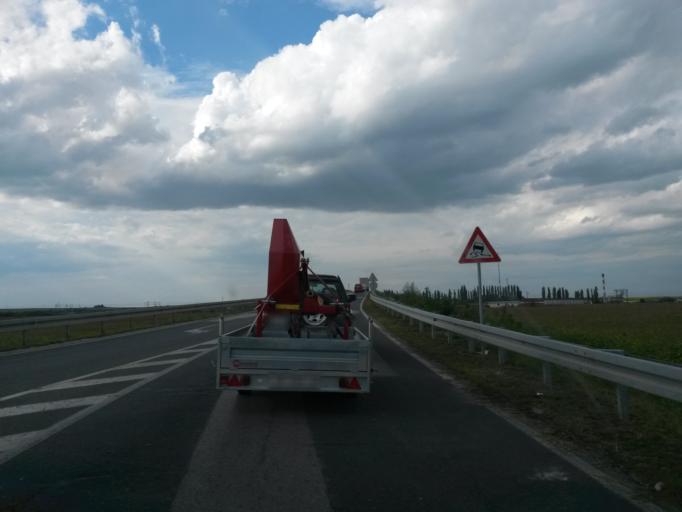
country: HR
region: Vukovarsko-Srijemska
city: Jarmina
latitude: 45.2879
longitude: 18.7425
